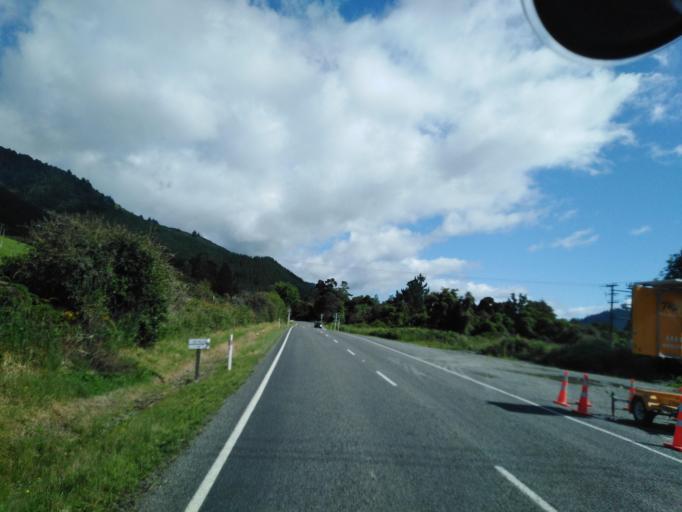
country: NZ
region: Nelson
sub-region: Nelson City
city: Nelson
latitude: -41.2936
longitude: 173.5737
